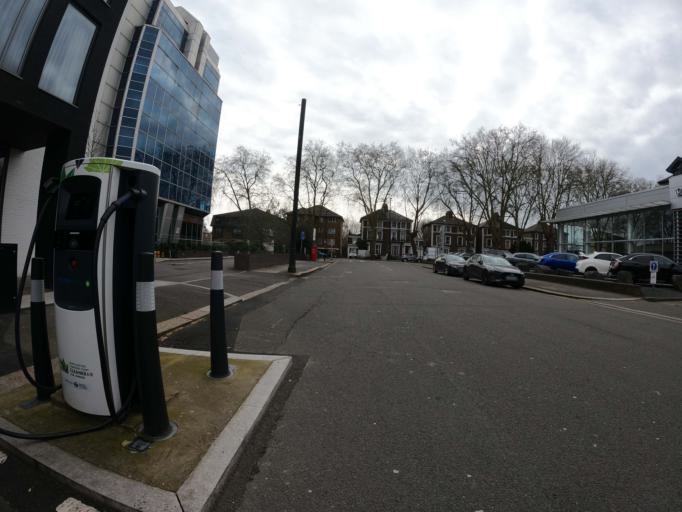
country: GB
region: England
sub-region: Greater London
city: Acton
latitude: 51.4926
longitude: -0.2790
